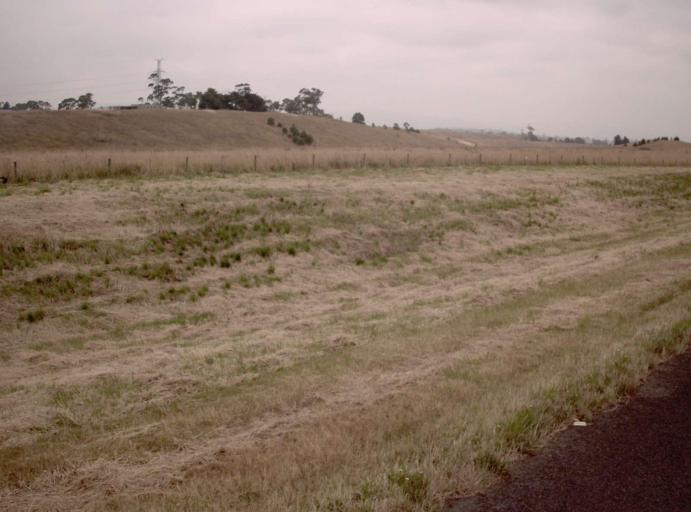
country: AU
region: Victoria
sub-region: Latrobe
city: Morwell
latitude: -38.2558
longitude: 146.3301
